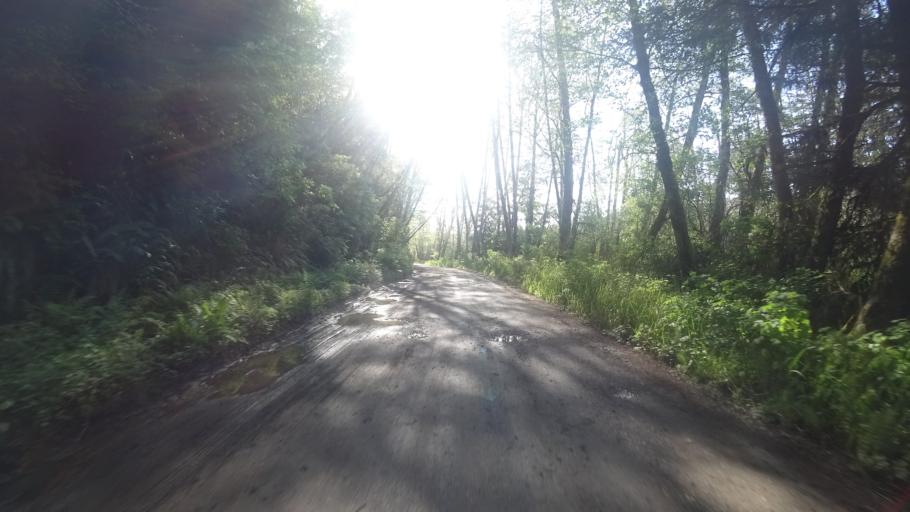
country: US
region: Oregon
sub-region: Douglas County
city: Reedsport
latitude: 43.7496
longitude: -124.1554
